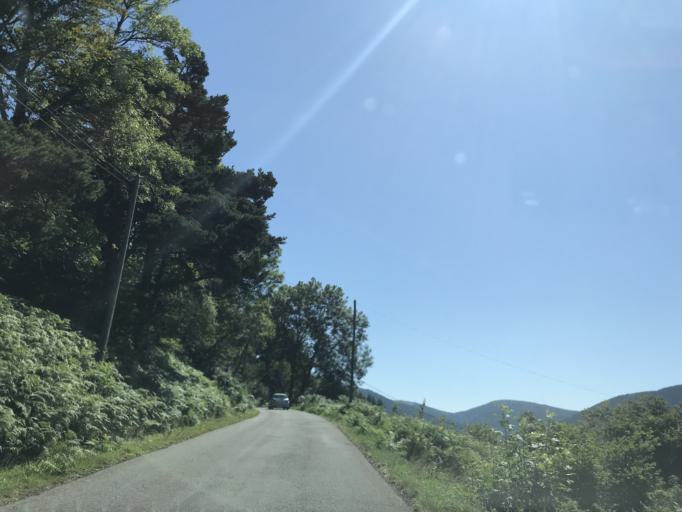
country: FR
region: Auvergne
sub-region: Departement du Puy-de-Dome
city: Job
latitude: 45.6785
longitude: 3.7491
